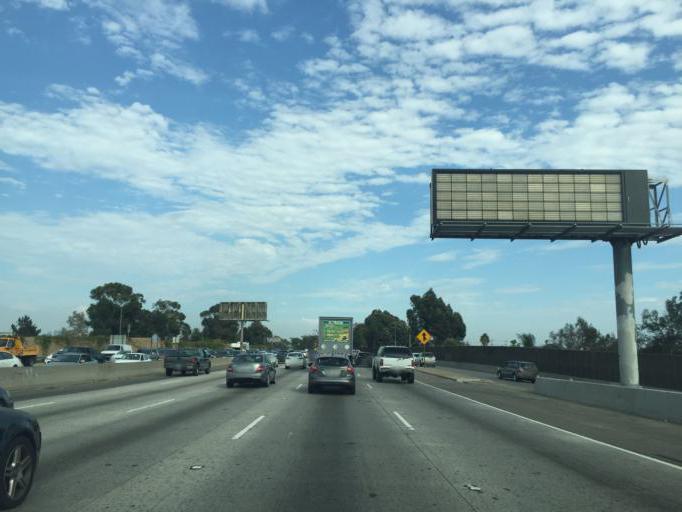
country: US
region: California
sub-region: Los Angeles County
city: Culver City
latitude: 34.0347
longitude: -118.3674
